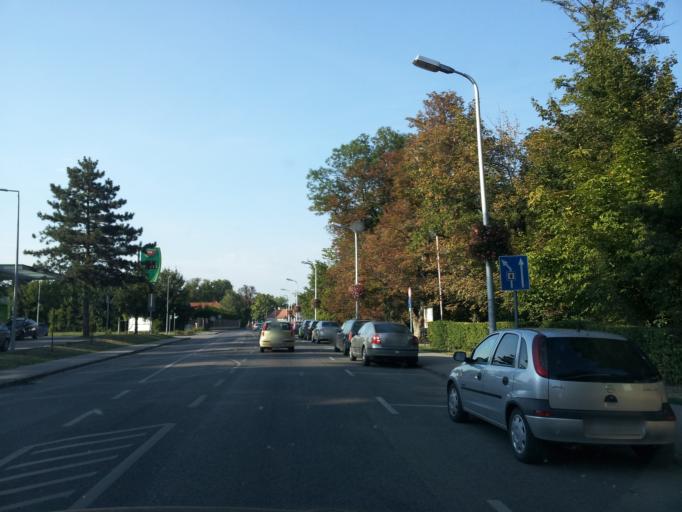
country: HU
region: Pest
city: Leanyfalu
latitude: 47.7164
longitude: 19.0891
